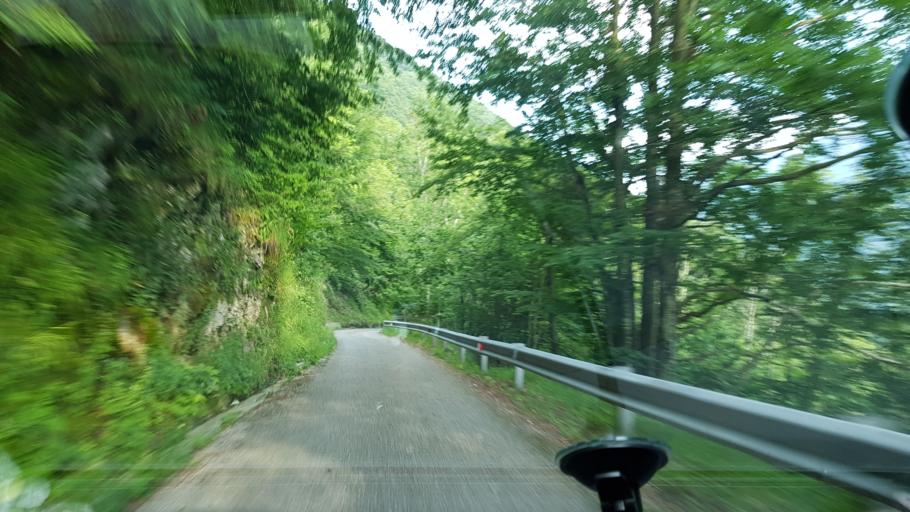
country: IT
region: Friuli Venezia Giulia
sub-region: Provincia di Udine
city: Taipana
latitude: 46.3210
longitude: 13.3878
